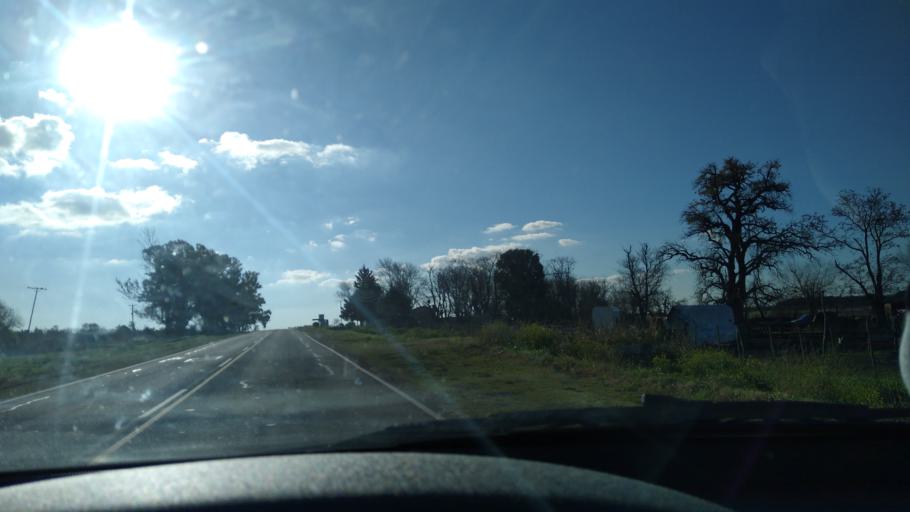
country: AR
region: Entre Rios
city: Diamante
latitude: -32.1141
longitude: -60.5737
